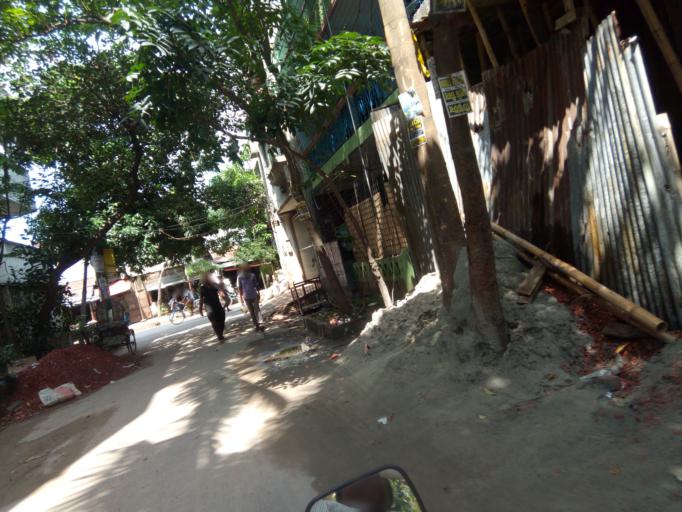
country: BD
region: Dhaka
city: Azimpur
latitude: 23.7630
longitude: 90.3623
